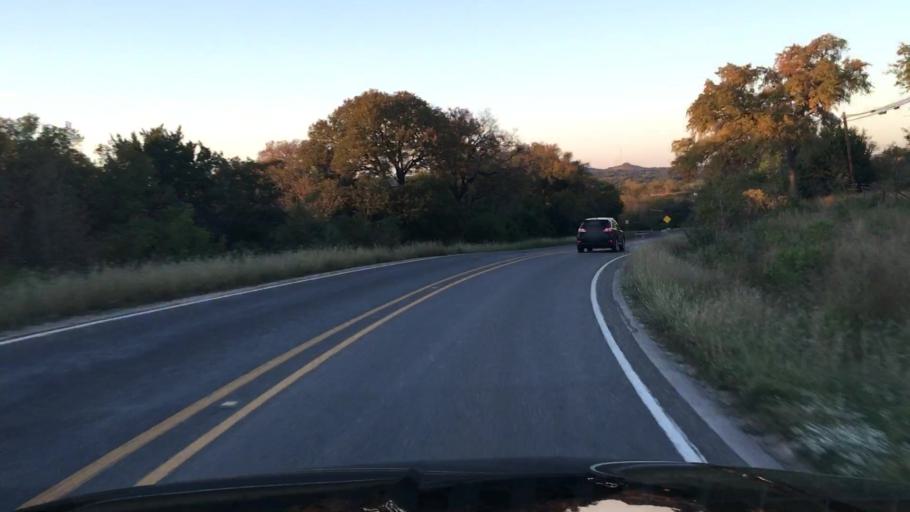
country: US
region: Texas
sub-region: Blanco County
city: Blanco
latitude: 30.0841
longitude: -98.4139
